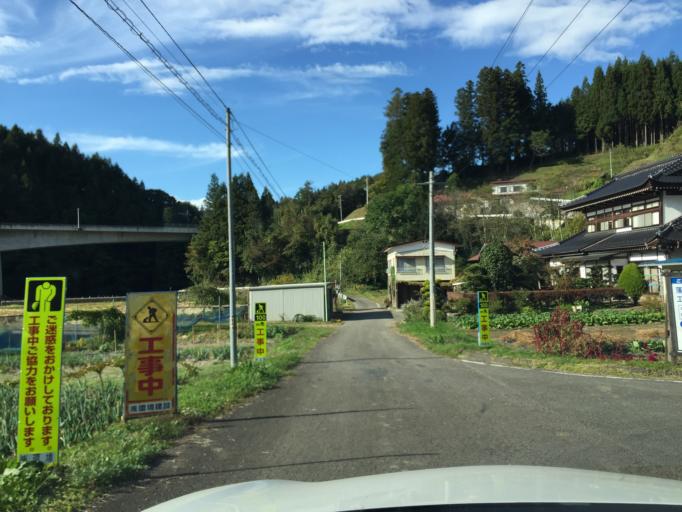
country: JP
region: Fukushima
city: Ishikawa
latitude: 37.1593
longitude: 140.5119
